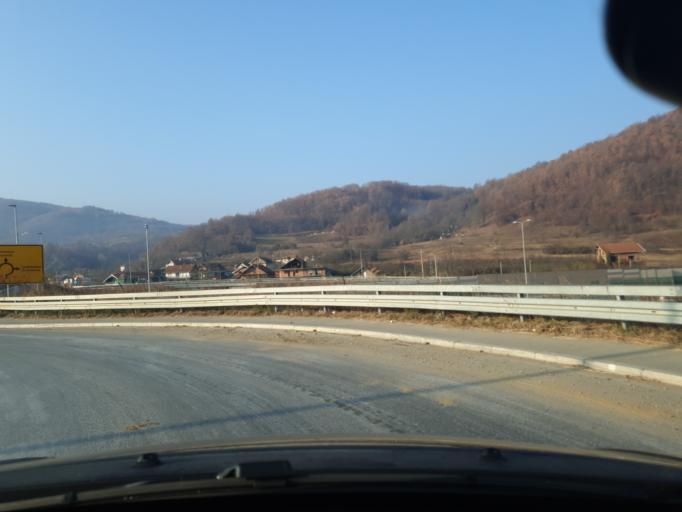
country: RS
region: Central Serbia
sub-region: Jablanicki Okrug
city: Vlasotince
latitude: 42.8869
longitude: 22.0658
